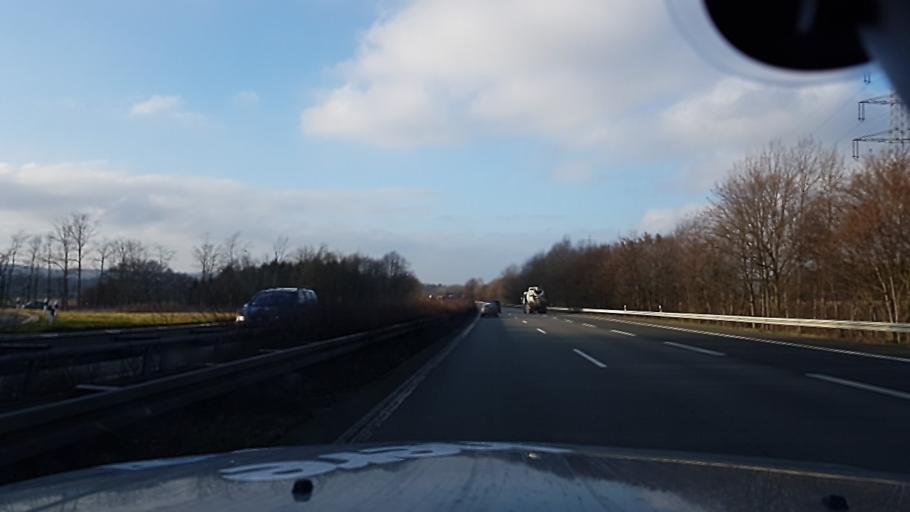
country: DE
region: North Rhine-Westphalia
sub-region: Regierungsbezirk Munster
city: Tecklenburg
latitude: 52.2572
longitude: 7.7728
